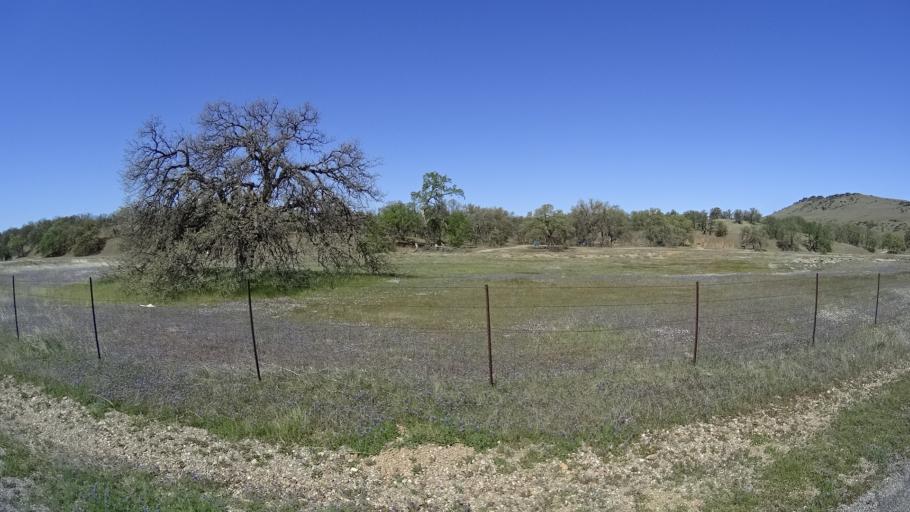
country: US
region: California
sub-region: Glenn County
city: Orland
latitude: 39.7600
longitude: -122.3435
